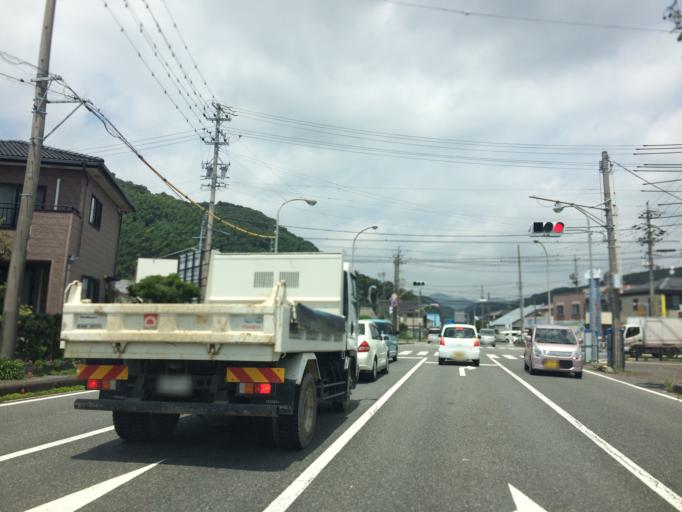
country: JP
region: Shizuoka
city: Shimada
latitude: 34.8362
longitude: 138.2002
